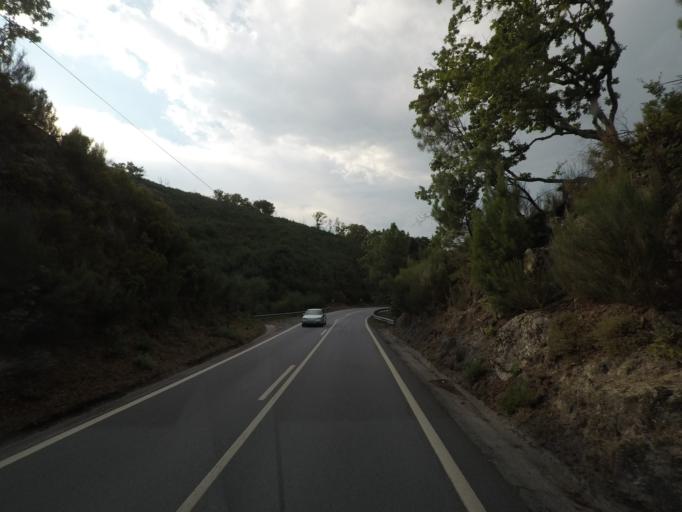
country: PT
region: Porto
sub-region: Baiao
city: Valadares
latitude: 41.2057
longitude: -7.9724
